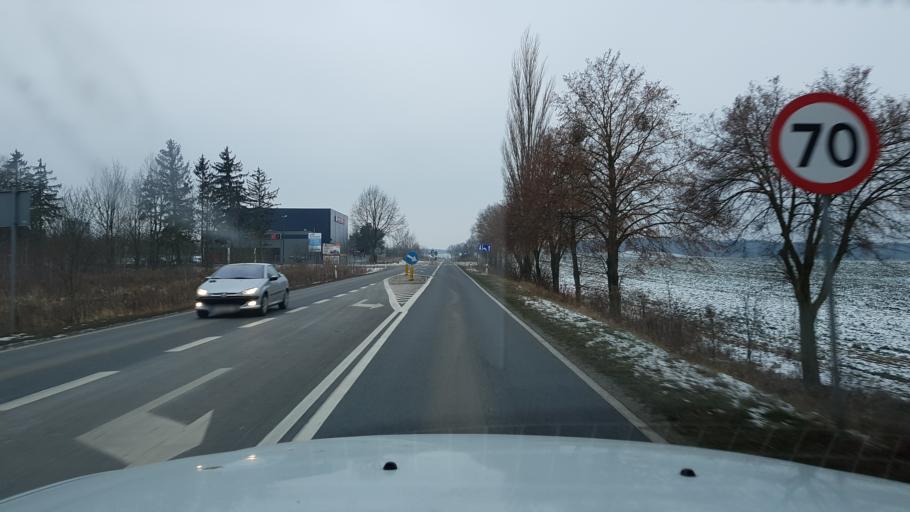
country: PL
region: West Pomeranian Voivodeship
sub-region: Powiat gryfinski
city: Chojna
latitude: 52.9535
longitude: 14.4094
